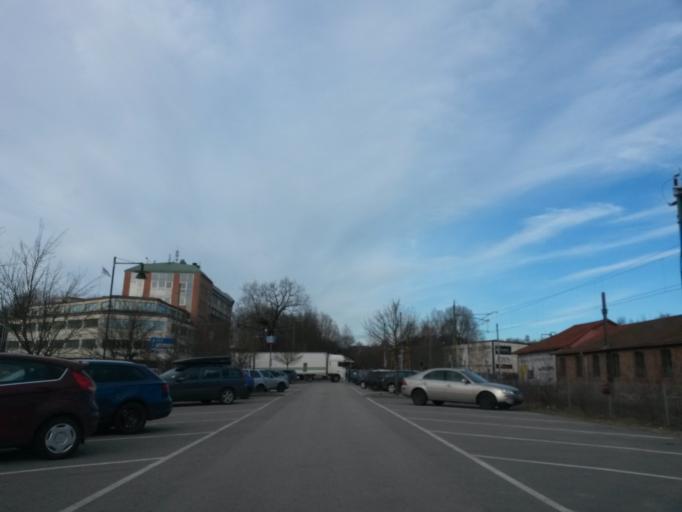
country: SE
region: Vaestra Goetaland
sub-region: Boras Kommun
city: Boras
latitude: 57.7293
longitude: 12.9406
